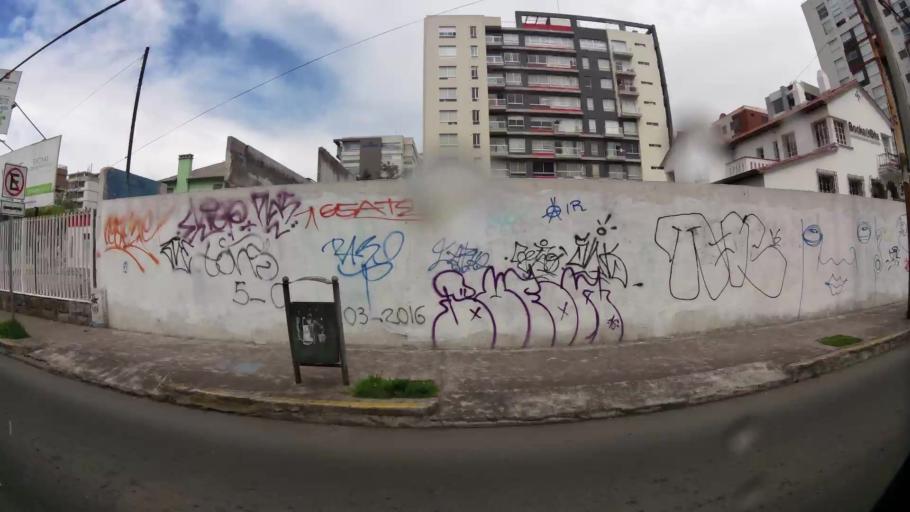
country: EC
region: Pichincha
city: Quito
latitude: -0.2058
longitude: -78.4923
